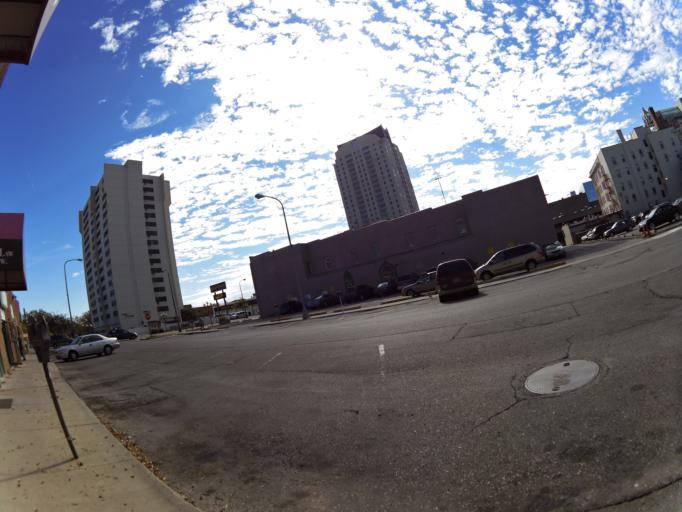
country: US
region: Minnesota
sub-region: Olmsted County
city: Rochester
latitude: 44.0245
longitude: -92.4643
